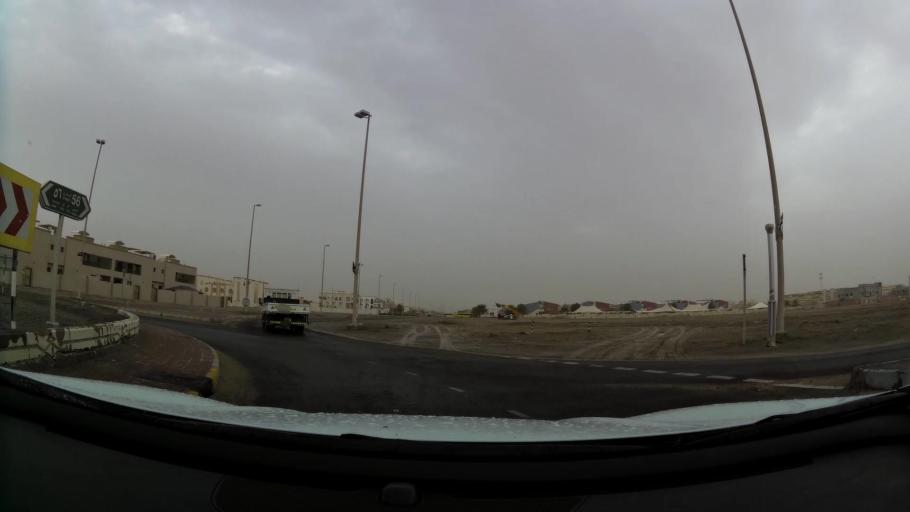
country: AE
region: Abu Dhabi
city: Abu Dhabi
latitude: 24.4082
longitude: 54.5879
